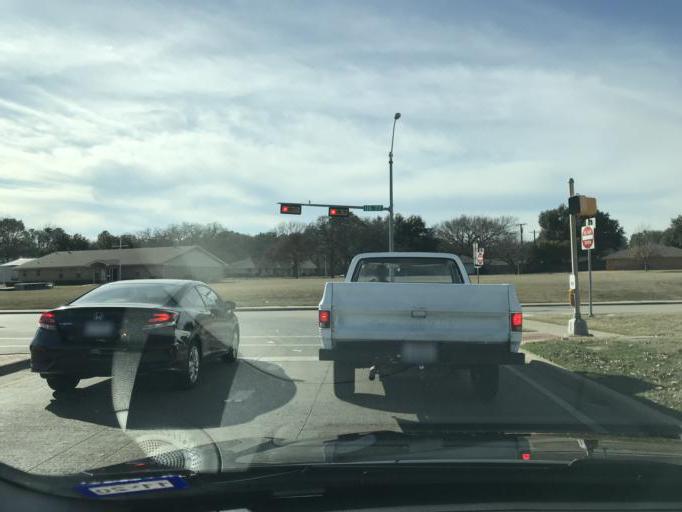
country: US
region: Texas
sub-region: Denton County
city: Denton
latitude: 33.2406
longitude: -97.1332
